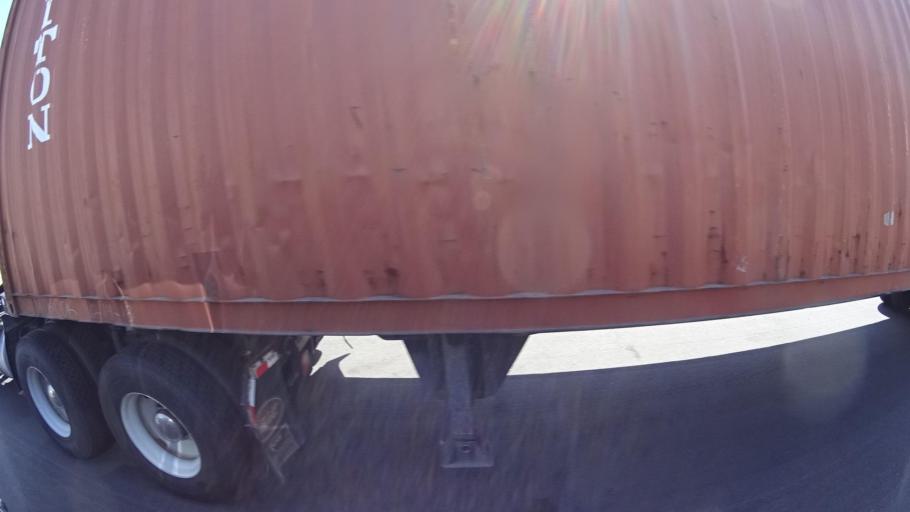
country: US
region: California
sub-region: Los Angeles County
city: South San Jose Hills
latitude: 34.0029
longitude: -117.9211
